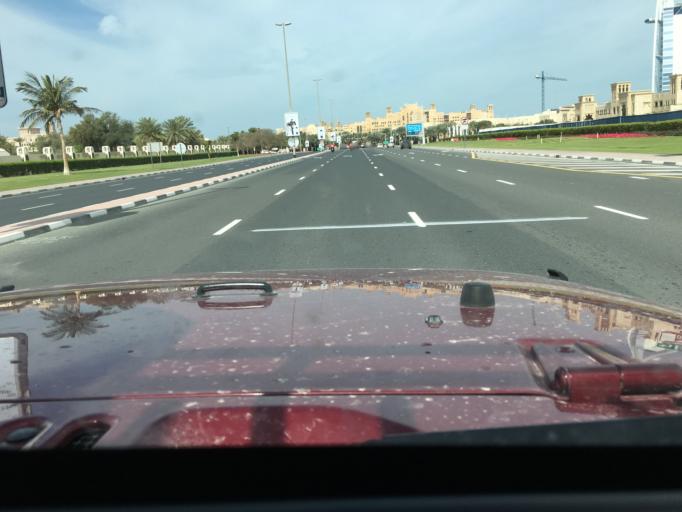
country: AE
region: Dubai
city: Dubai
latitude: 25.1312
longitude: 55.1906
